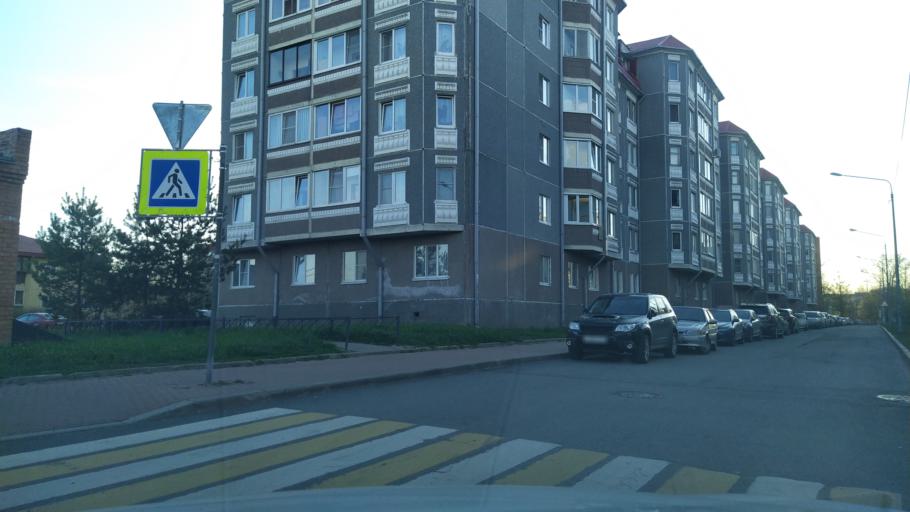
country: RU
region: St.-Petersburg
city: Pushkin
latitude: 59.7035
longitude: 30.3772
